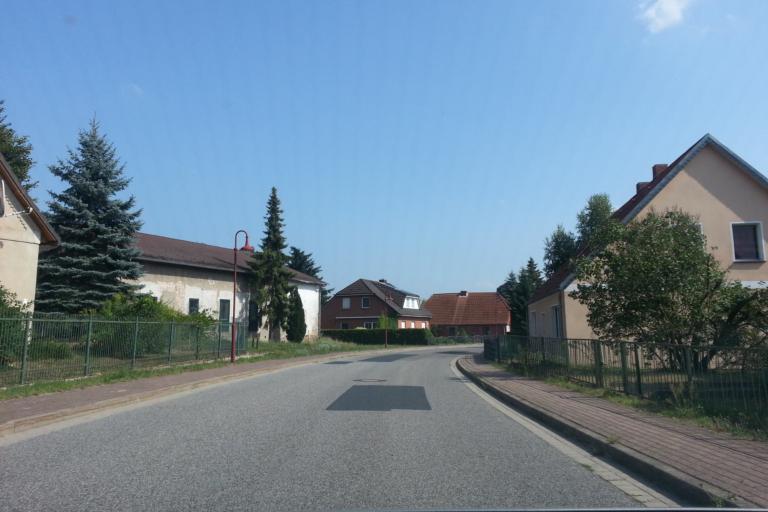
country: DE
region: Mecklenburg-Vorpommern
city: Ferdinandshof
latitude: 53.5975
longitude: 13.8163
